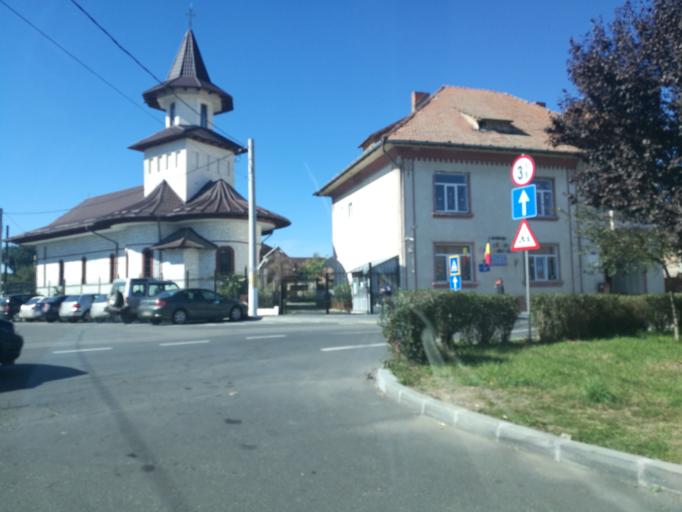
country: RO
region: Brasov
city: Fogarasch
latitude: 45.8411
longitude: 24.9727
